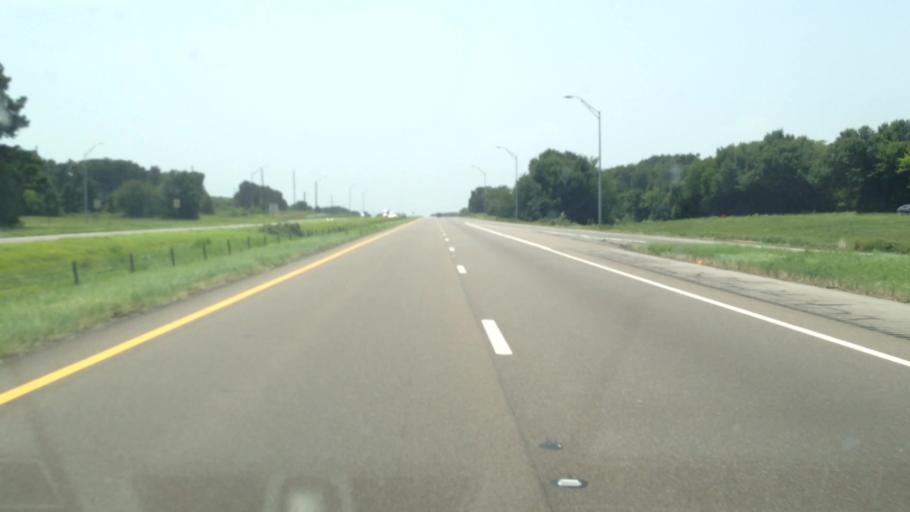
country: US
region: Texas
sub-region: Titus County
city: Mount Pleasant
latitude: 33.1588
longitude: -95.0501
